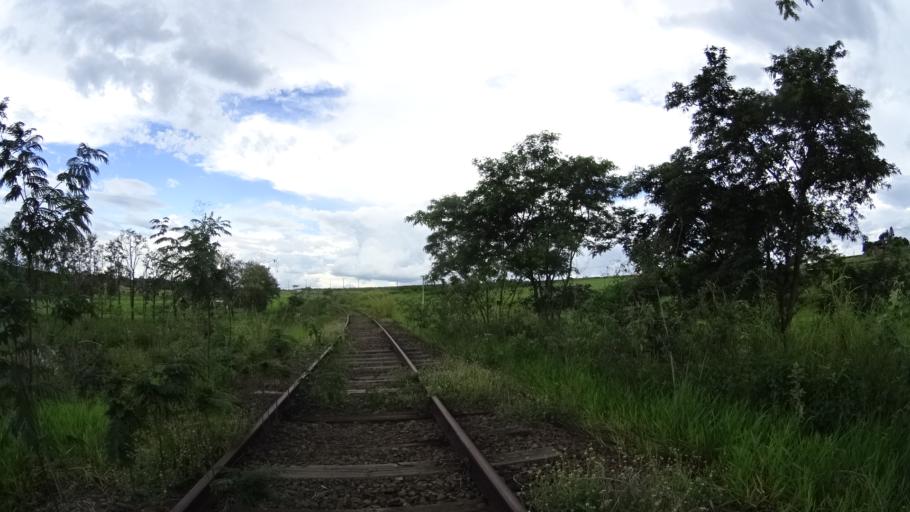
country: BR
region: Sao Paulo
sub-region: Marilia
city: Marilia
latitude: -22.2183
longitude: -49.8645
